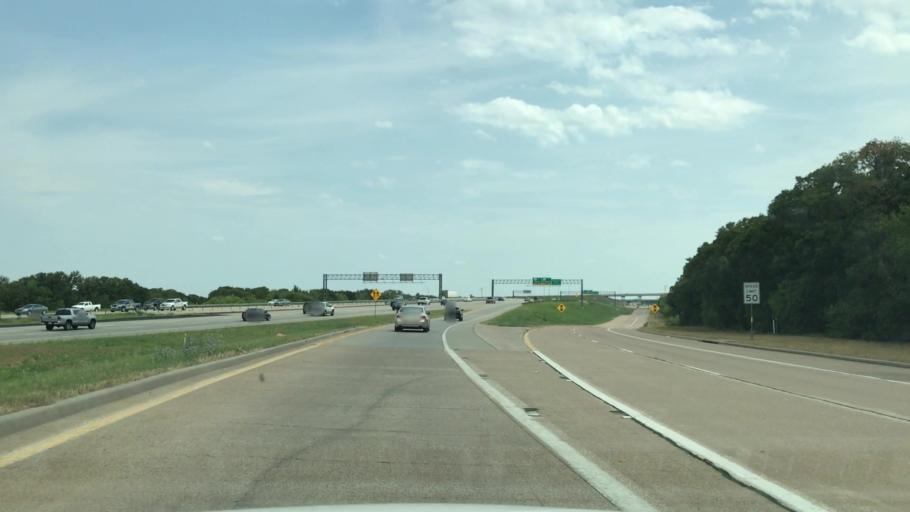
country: US
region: Texas
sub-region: Tarrant County
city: Euless
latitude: 32.8494
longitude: -97.0642
